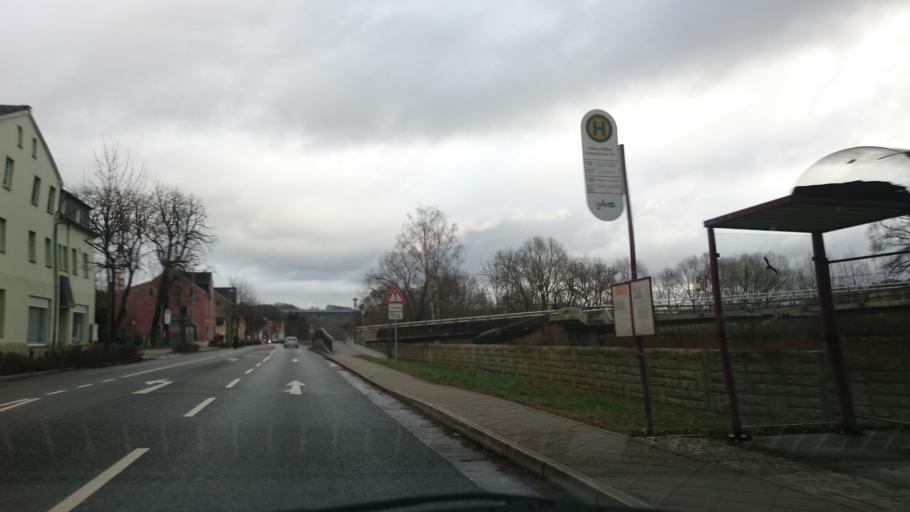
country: DE
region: Saxony
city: Wilkau-Hasslau
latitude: 50.6764
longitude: 12.5146
